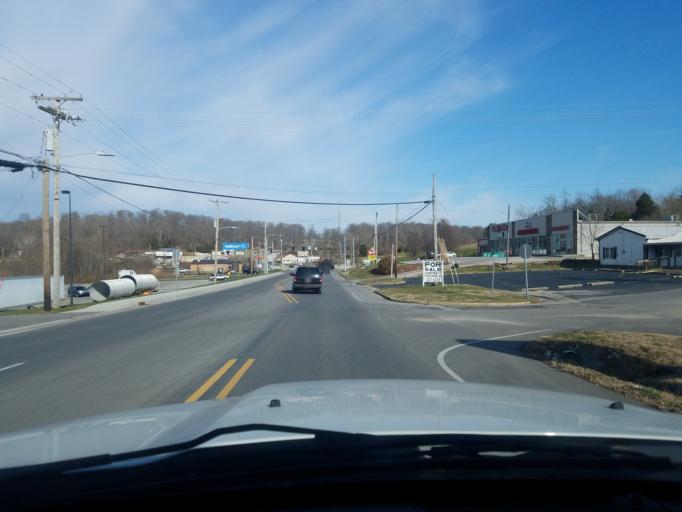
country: US
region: Indiana
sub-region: Orange County
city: Paoli
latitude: 38.5639
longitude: -86.4662
